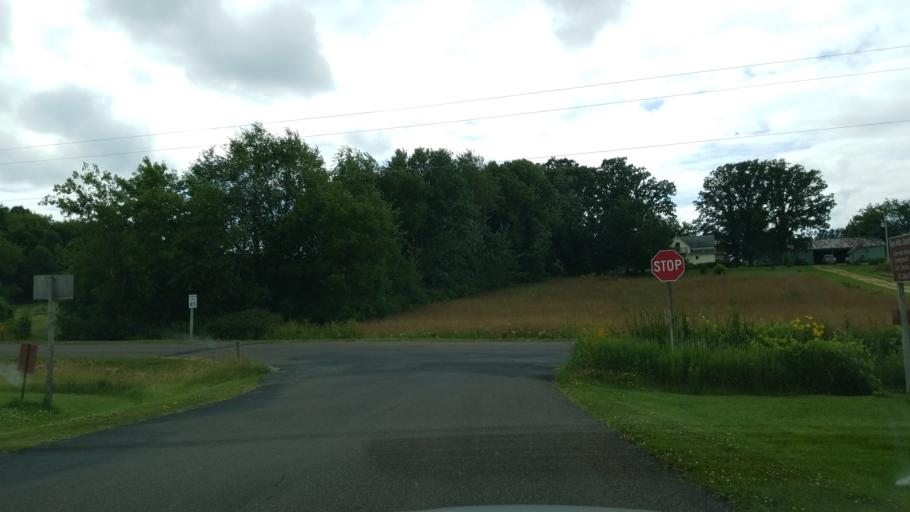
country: US
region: Wisconsin
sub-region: Saint Croix County
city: Glenwood City
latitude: 44.9992
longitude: -92.1760
